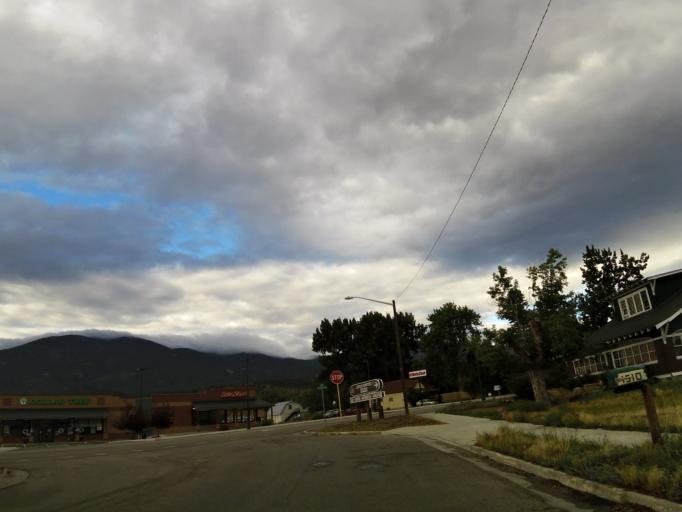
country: US
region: Colorado
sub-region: Chaffee County
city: Salida
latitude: 38.5245
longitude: -106.0034
